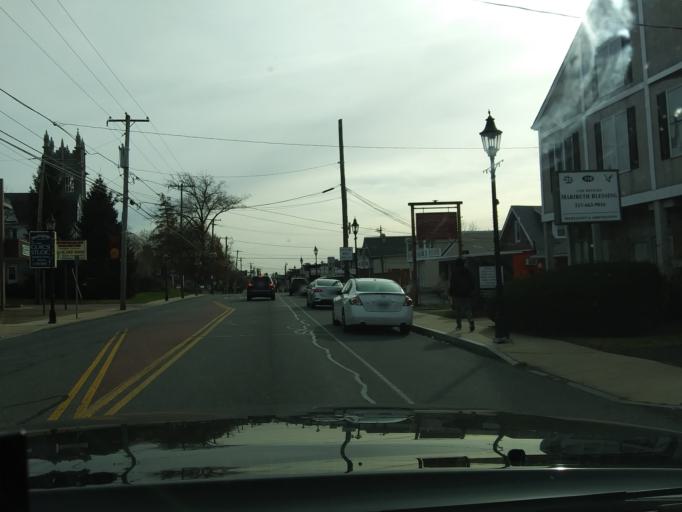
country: US
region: Pennsylvania
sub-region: Montgomery County
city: Rockledge
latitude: 40.0811
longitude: -75.0897
